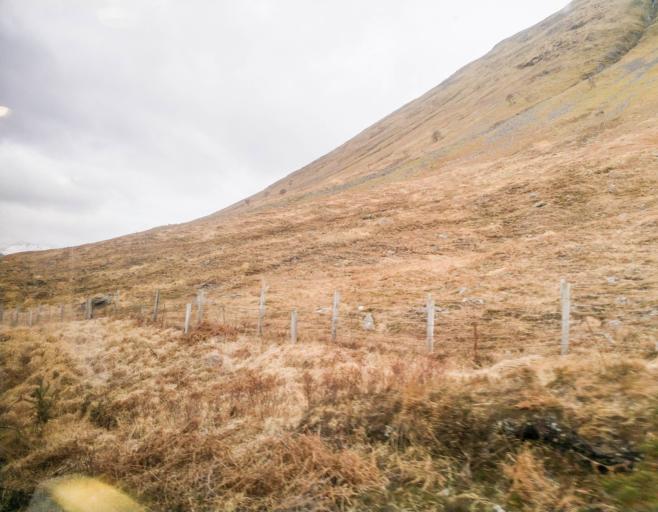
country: GB
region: Scotland
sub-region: Argyll and Bute
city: Garelochhead
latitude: 56.4886
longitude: -4.7254
